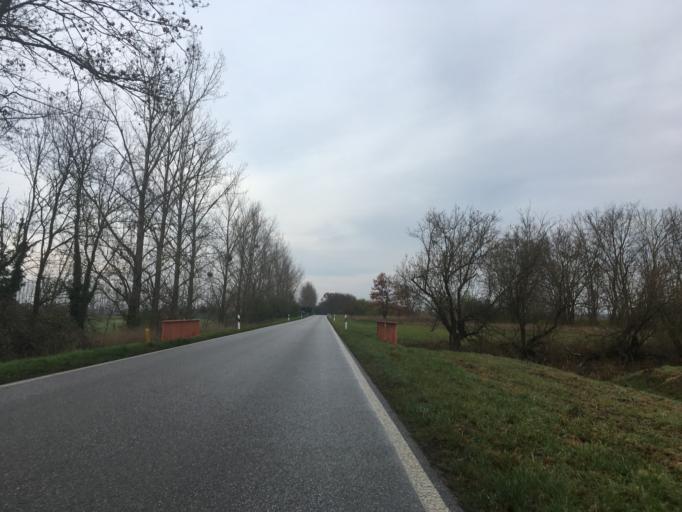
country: DE
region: Brandenburg
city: Letschin
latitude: 52.6805
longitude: 14.4025
